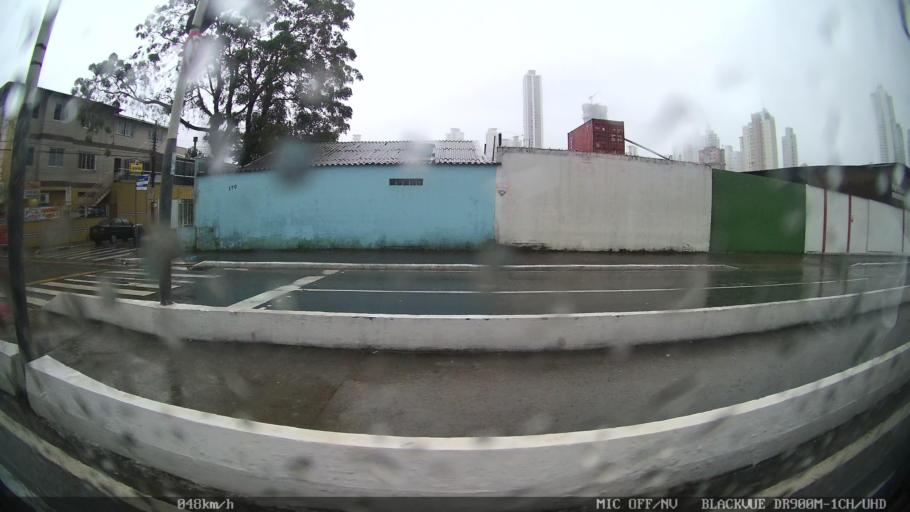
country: BR
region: Santa Catarina
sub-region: Balneario Camboriu
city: Balneario Camboriu
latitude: -27.0064
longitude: -48.6259
